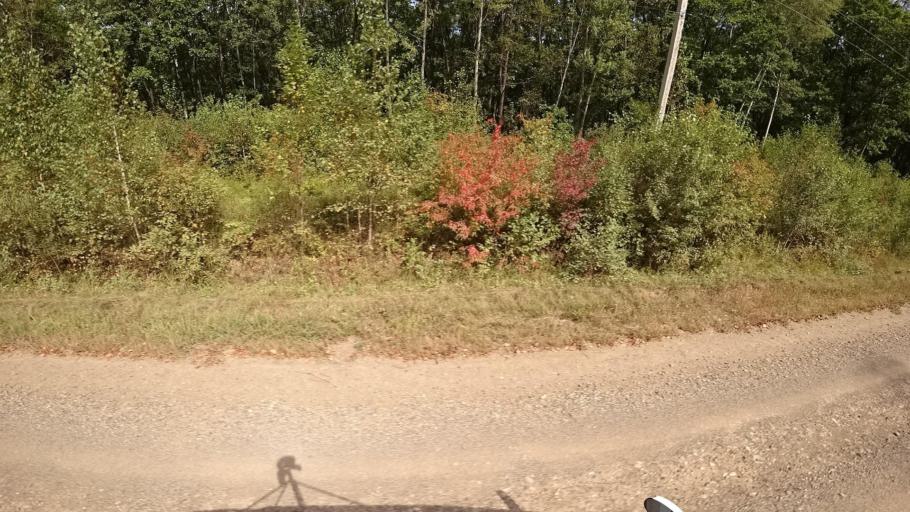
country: RU
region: Primorskiy
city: Yakovlevka
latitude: 44.7108
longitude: 133.6255
